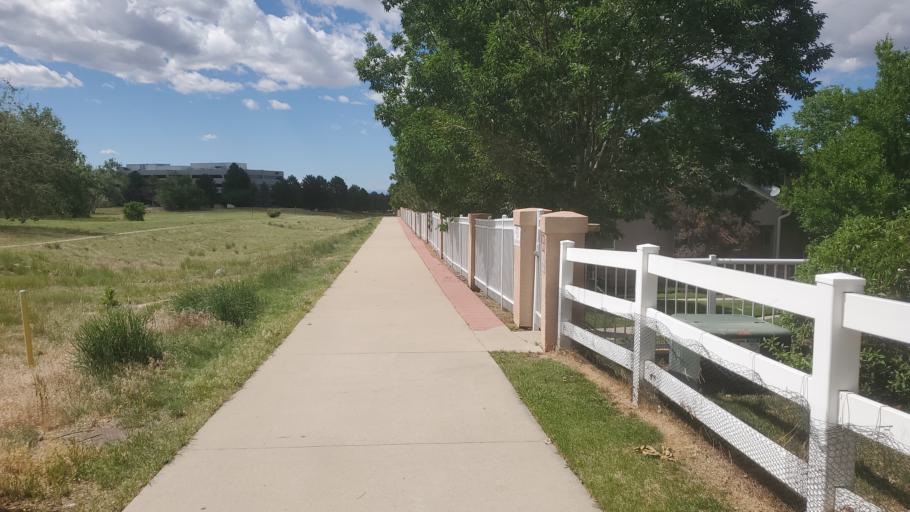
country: US
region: Colorado
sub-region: Adams County
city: Aurora
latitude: 39.6712
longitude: -104.8424
